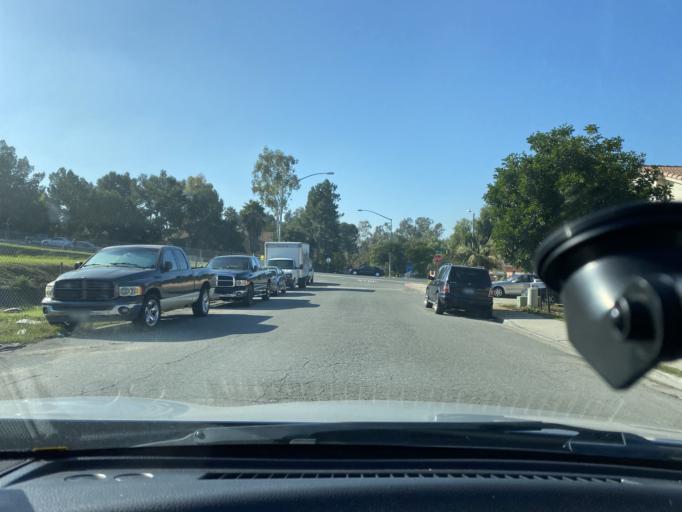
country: US
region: California
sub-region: San Diego County
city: National City
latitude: 32.7060
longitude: -117.0930
